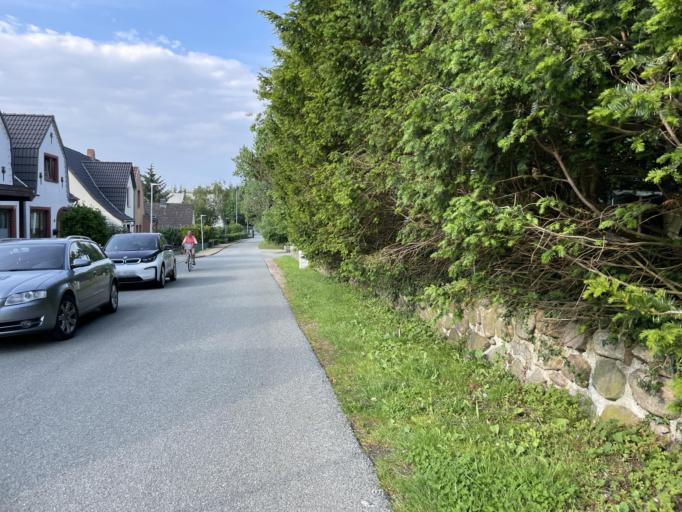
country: DE
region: Schleswig-Holstein
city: Husum
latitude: 54.4698
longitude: 9.0673
